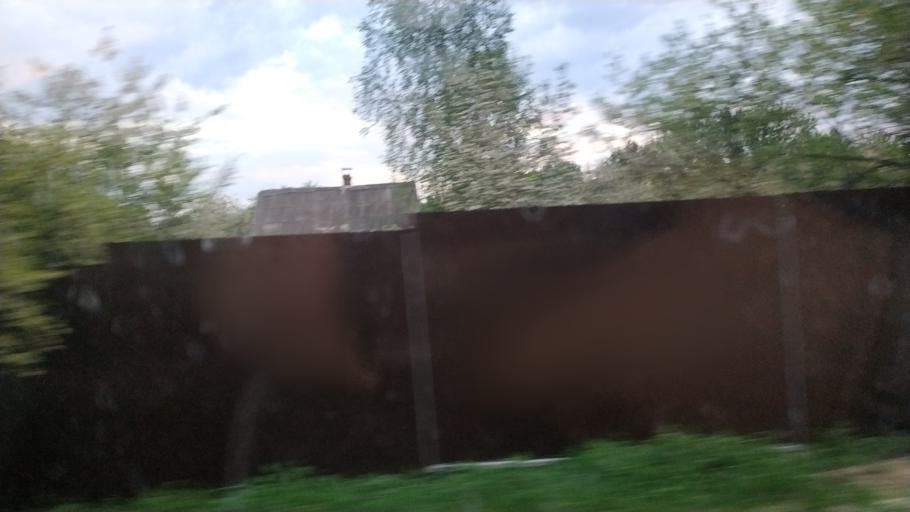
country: RU
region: Moskovskaya
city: Kashira
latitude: 54.8444
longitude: 38.1709
